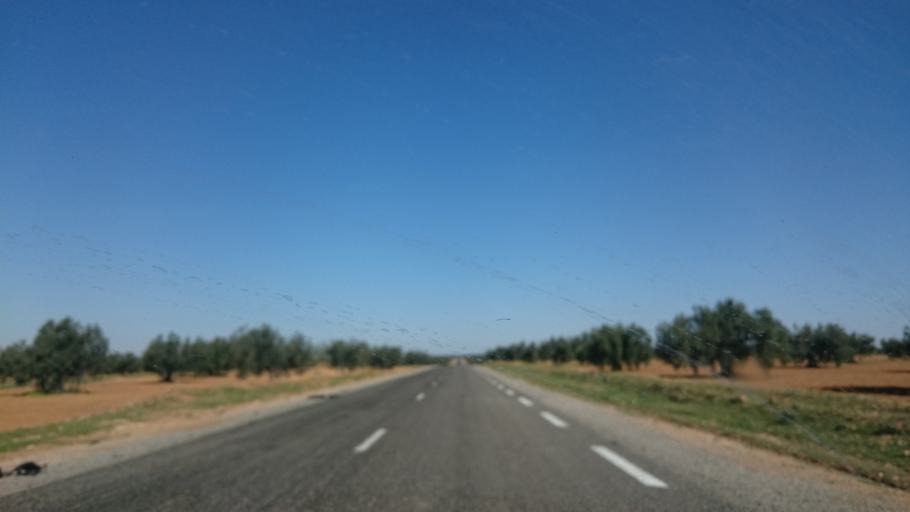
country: TN
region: Safaqis
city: Sfax
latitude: 34.8209
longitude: 10.4721
